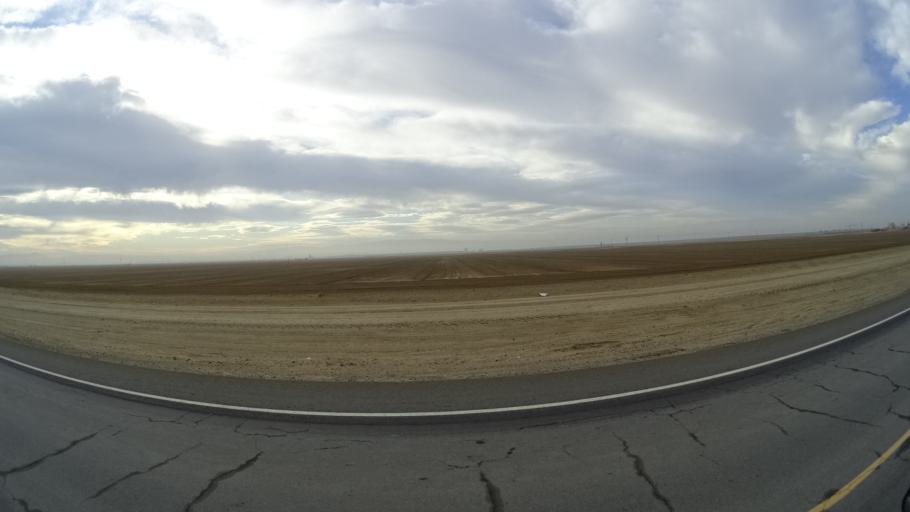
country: US
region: California
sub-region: Kern County
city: Rosedale
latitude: 35.4198
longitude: -119.2242
